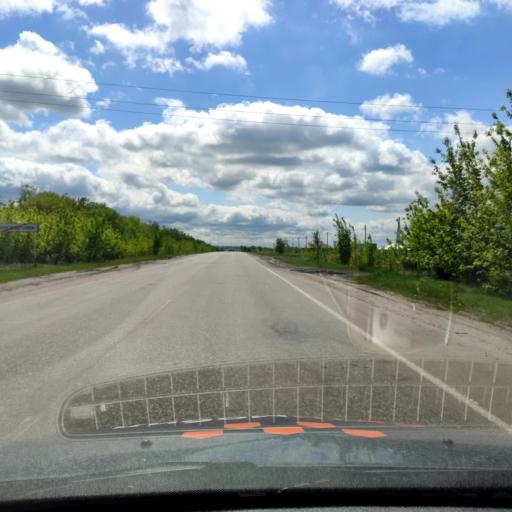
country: RU
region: Voronezj
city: Novaya Usman'
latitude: 51.6170
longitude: 39.3363
